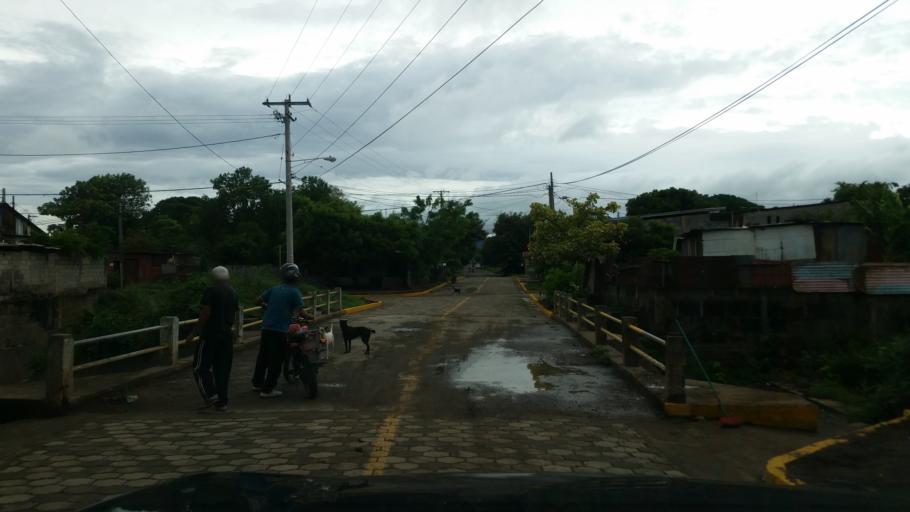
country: NI
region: Granada
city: Granada
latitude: 11.9472
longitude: -85.9531
